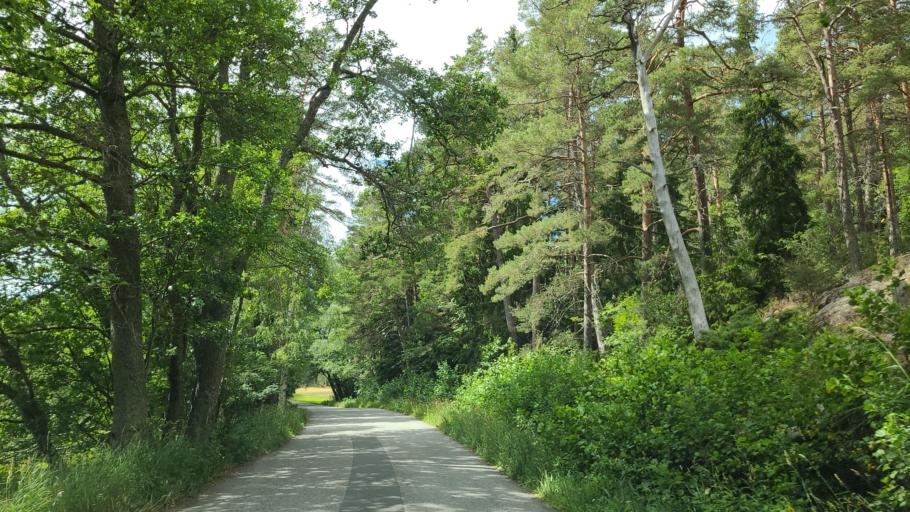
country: FI
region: Varsinais-Suomi
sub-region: Aboland-Turunmaa
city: Nagu
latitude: 60.1654
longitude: 21.9894
